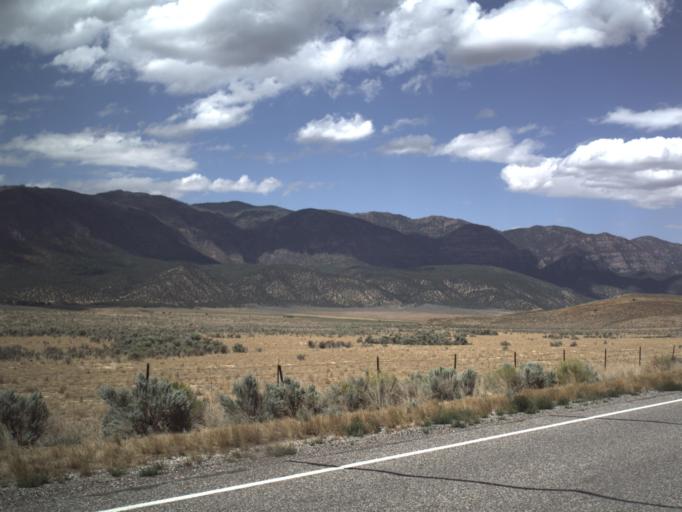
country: US
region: Utah
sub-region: Sevier County
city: Aurora
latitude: 39.0171
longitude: -112.0329
